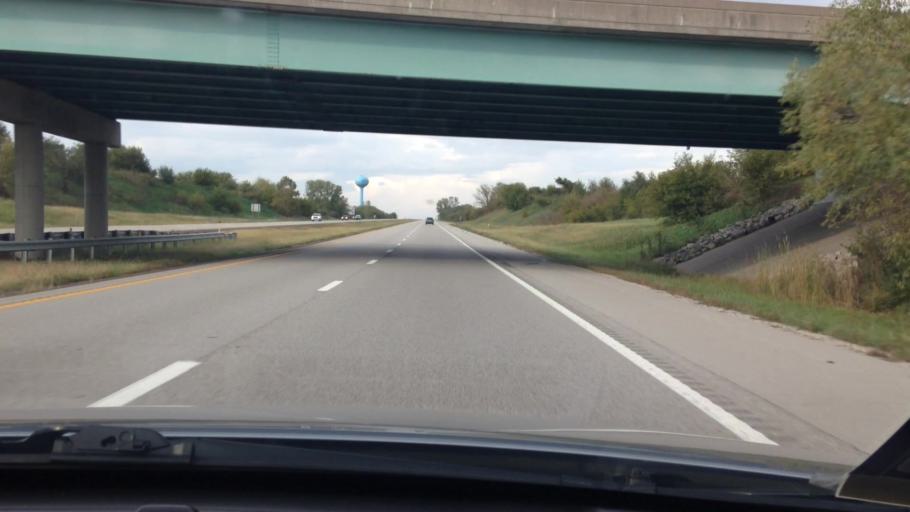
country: US
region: Missouri
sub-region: Platte County
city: Platte City
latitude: 39.3103
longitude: -94.7580
